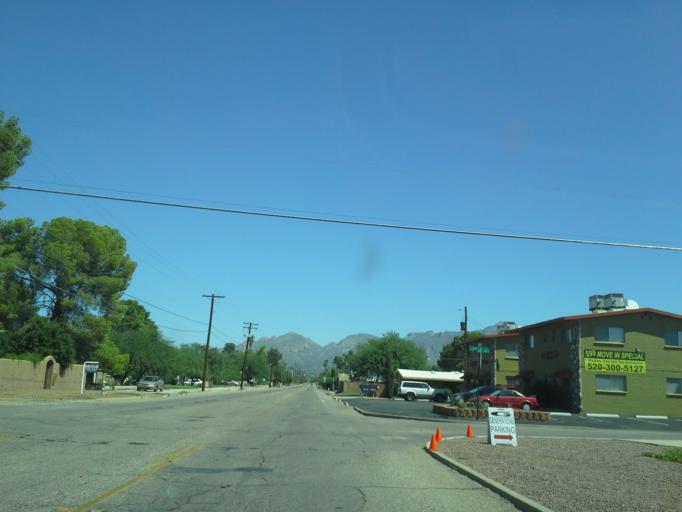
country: US
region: Arizona
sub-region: Pima County
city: Tucson
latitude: 32.2537
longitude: -110.9353
